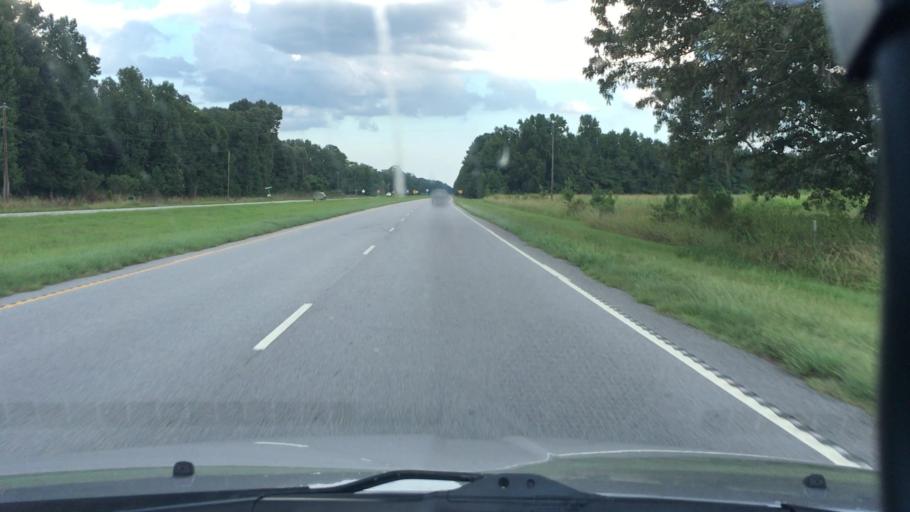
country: US
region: South Carolina
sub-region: Hampton County
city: Yemassee
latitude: 32.6366
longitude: -80.8441
